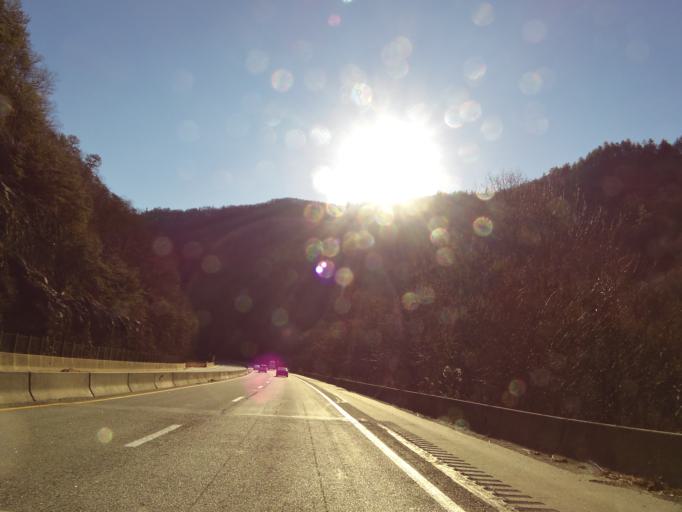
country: US
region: North Carolina
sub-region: Haywood County
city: Cove Creek
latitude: 35.7524
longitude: -83.0668
